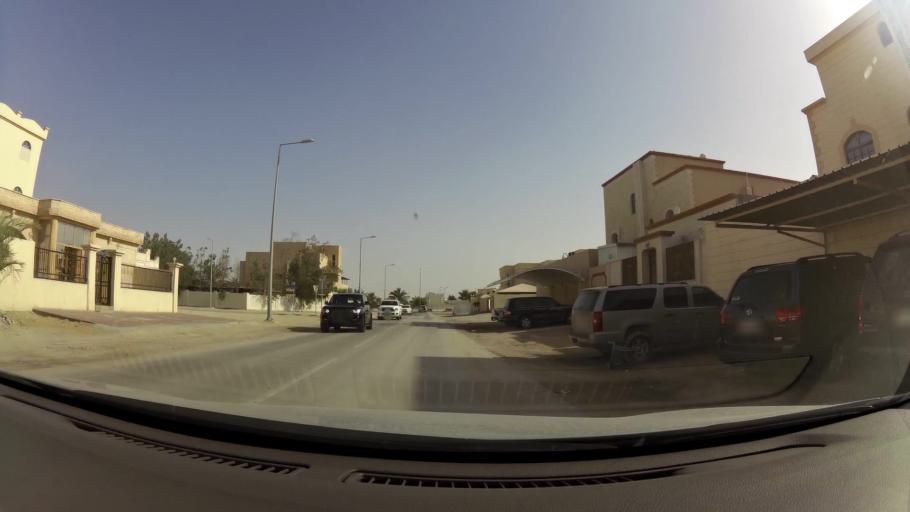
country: QA
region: Baladiyat ar Rayyan
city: Ar Rayyan
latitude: 25.3411
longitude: 51.4287
